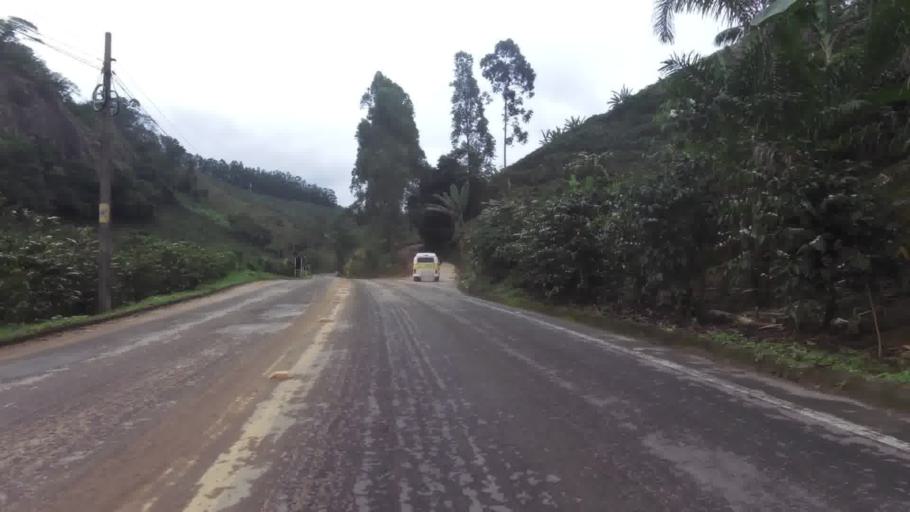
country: BR
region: Espirito Santo
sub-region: Iconha
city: Iconha
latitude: -20.7532
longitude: -40.8372
